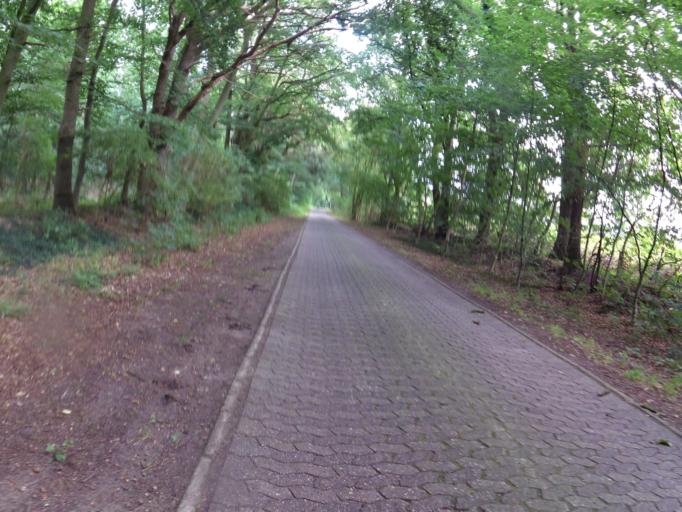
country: DE
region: Lower Saxony
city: Kohlen
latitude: 53.5056
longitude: 8.9087
